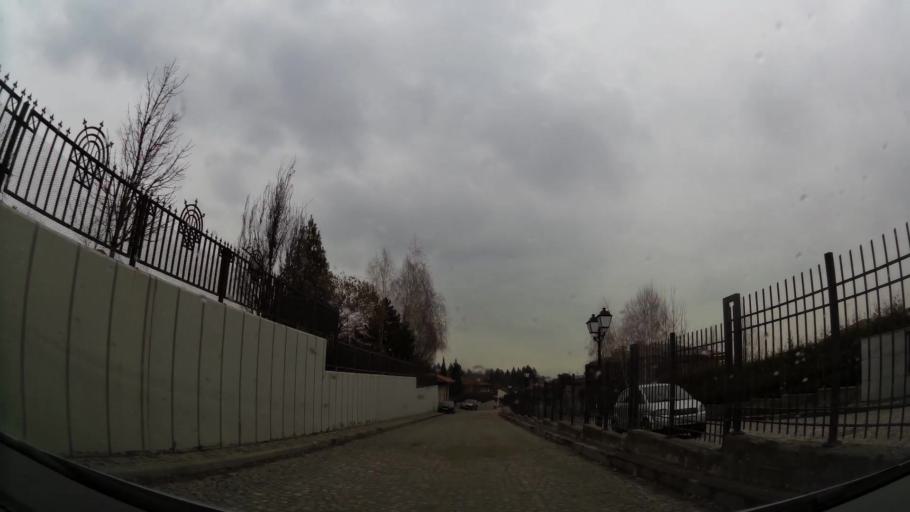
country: BG
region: Sofia-Capital
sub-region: Stolichna Obshtina
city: Sofia
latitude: 42.6141
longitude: 23.3749
